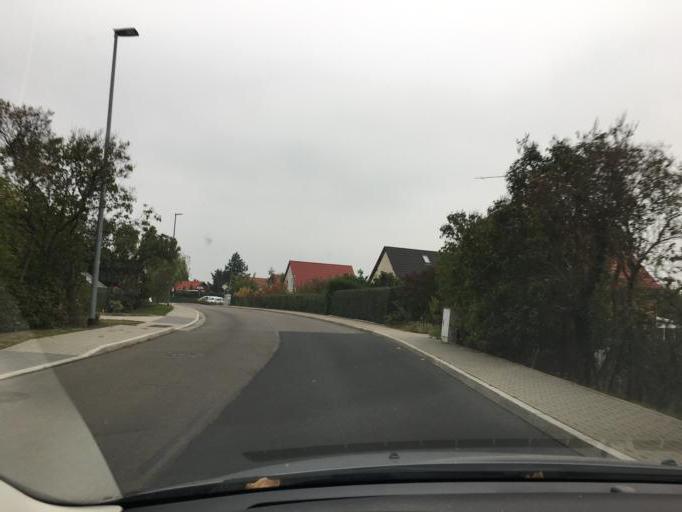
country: DE
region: Saxony
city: Freital
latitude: 51.0001
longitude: 13.6820
